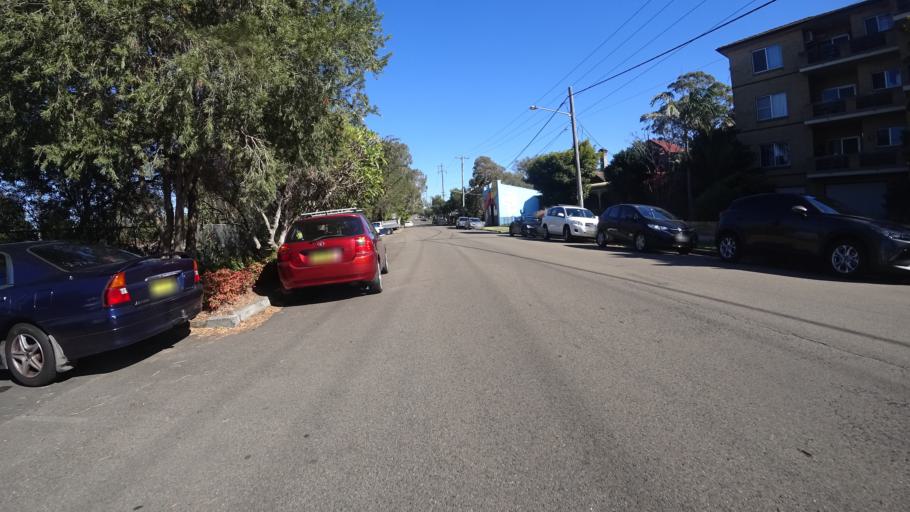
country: AU
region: New South Wales
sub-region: Kogarah
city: Kogarah Bay
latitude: -33.9684
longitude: 151.1227
